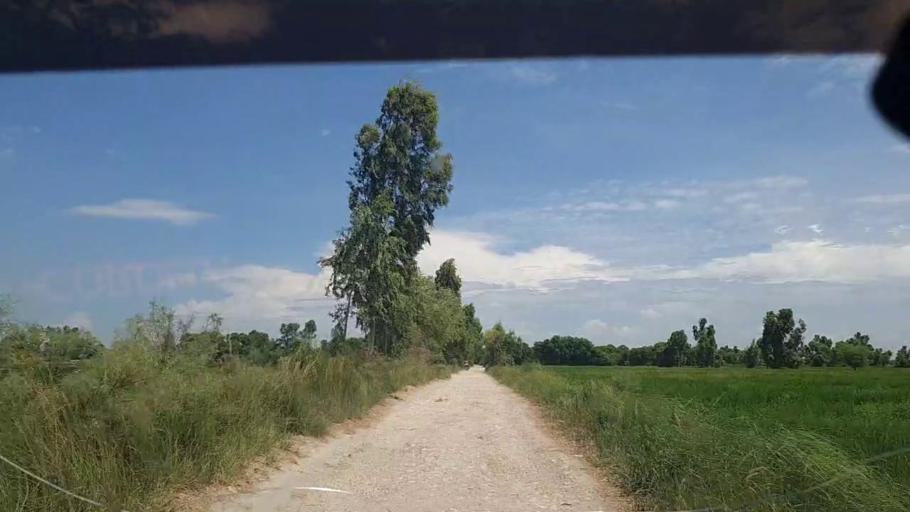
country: PK
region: Sindh
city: Ghauspur
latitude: 28.1500
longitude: 68.9523
